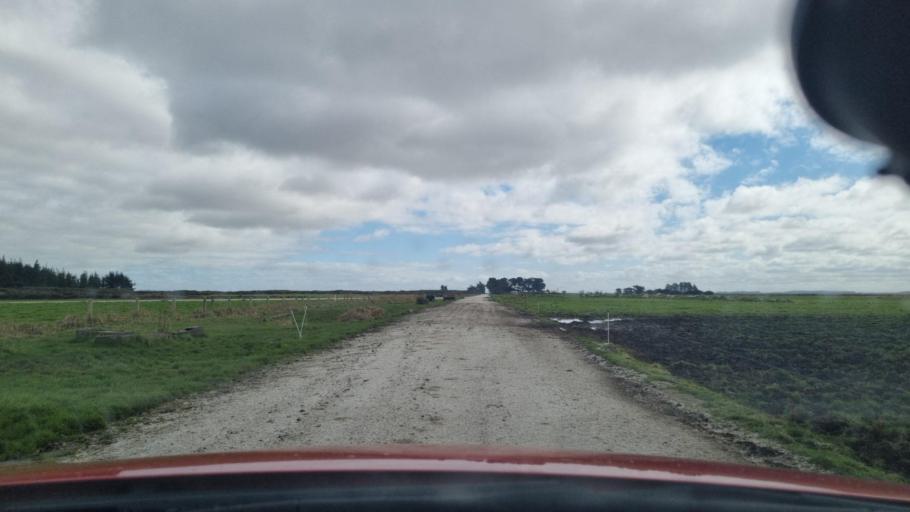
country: NZ
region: Southland
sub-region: Invercargill City
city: Bluff
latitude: -46.5620
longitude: 168.4934
